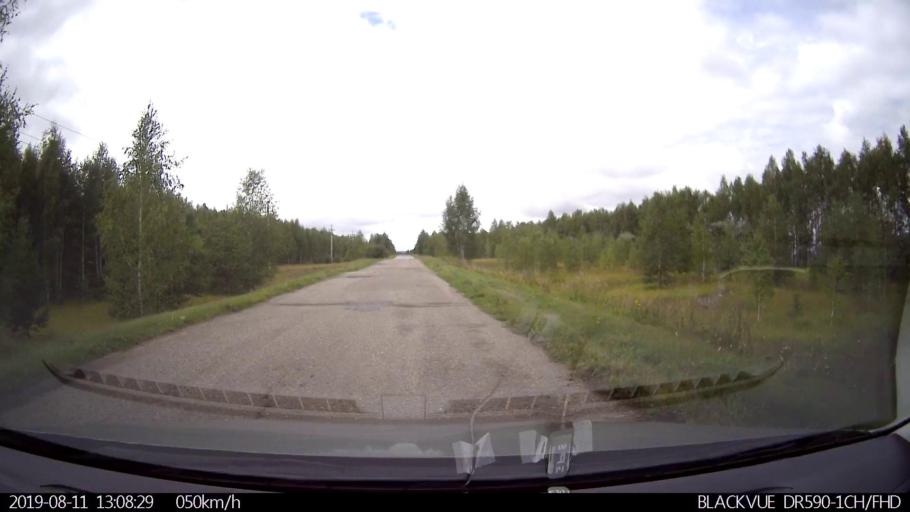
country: RU
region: Ulyanovsk
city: Ignatovka
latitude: 53.8589
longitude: 47.6334
